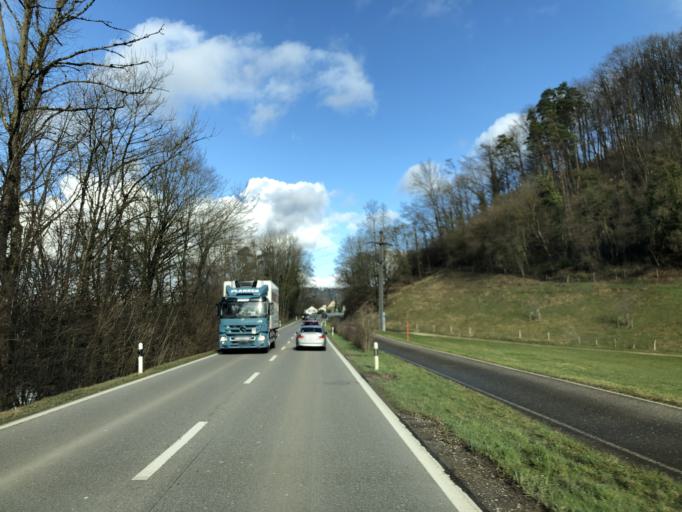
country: CH
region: Aargau
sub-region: Bezirk Baden
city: Gebenstorf
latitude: 47.4723
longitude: 8.2339
